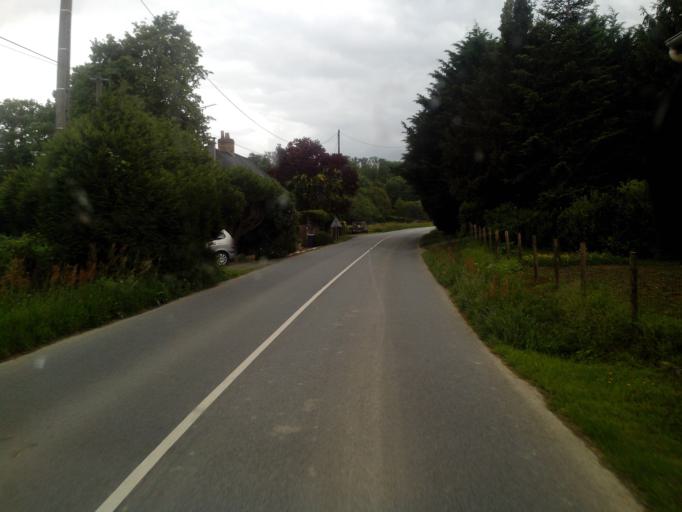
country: FR
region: Brittany
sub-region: Departement d'Ille-et-Vilaine
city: Chasne-sur-Illet
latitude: 48.2399
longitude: -1.5467
